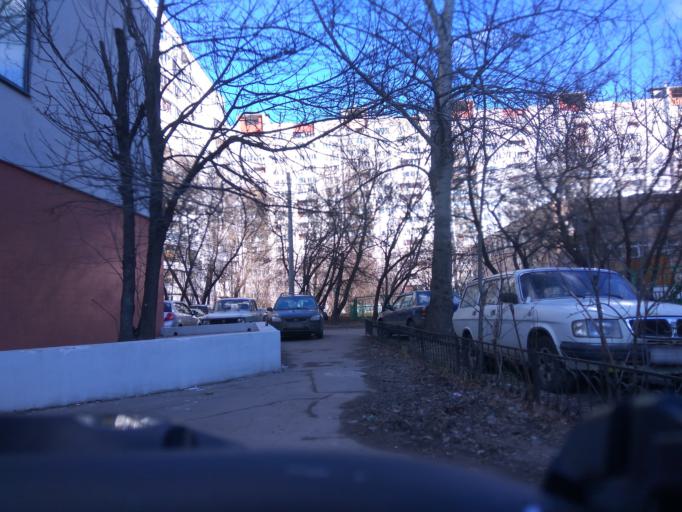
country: RU
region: Moscow
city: Ostankinskiy
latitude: 55.8180
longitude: 37.6206
